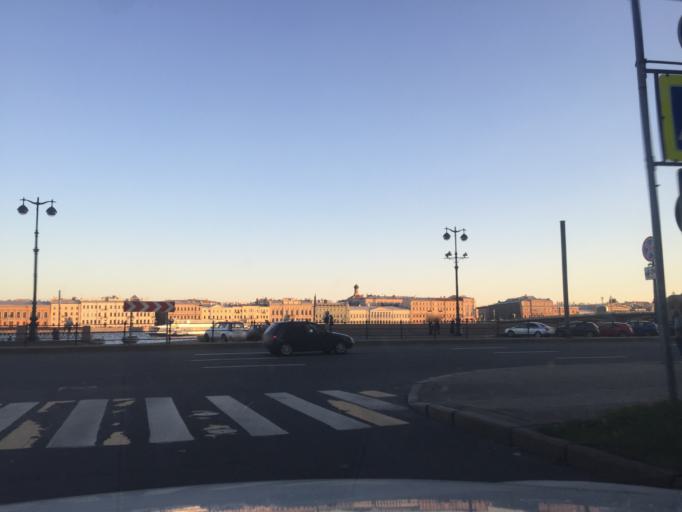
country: RU
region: St.-Petersburg
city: Saint Petersburg
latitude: 59.9380
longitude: 30.2915
